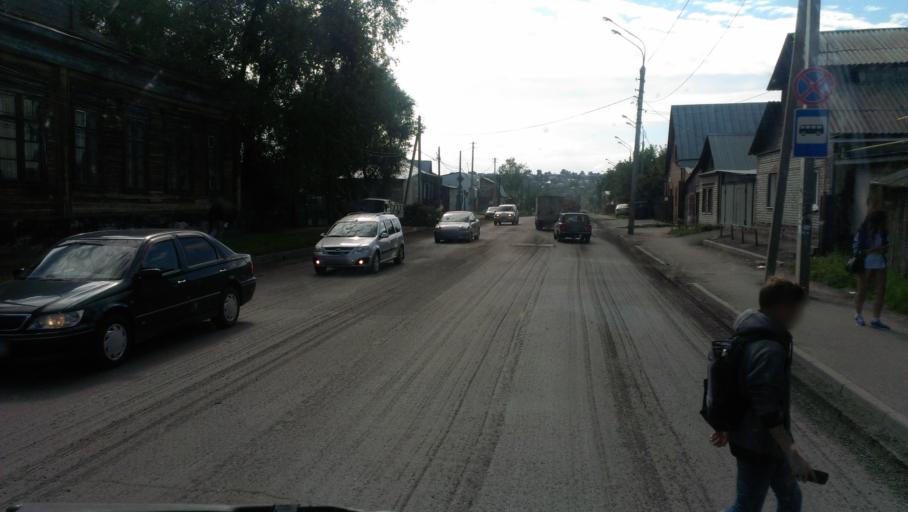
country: RU
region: Altai Krai
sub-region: Gorod Barnaulskiy
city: Barnaul
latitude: 53.3270
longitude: 83.7635
